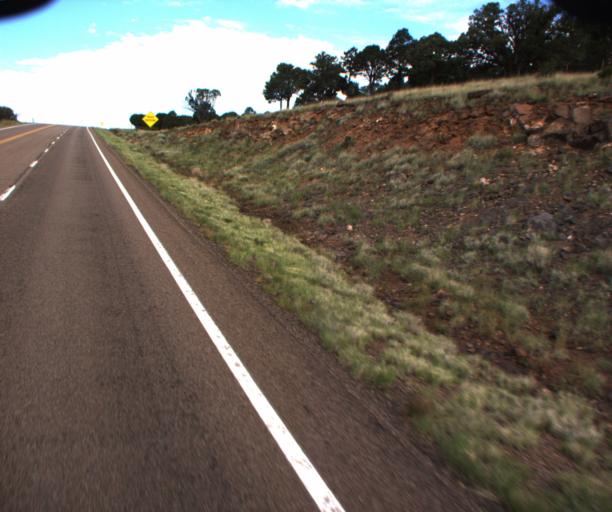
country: US
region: Arizona
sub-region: Apache County
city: Springerville
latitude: 34.2654
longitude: -109.5750
